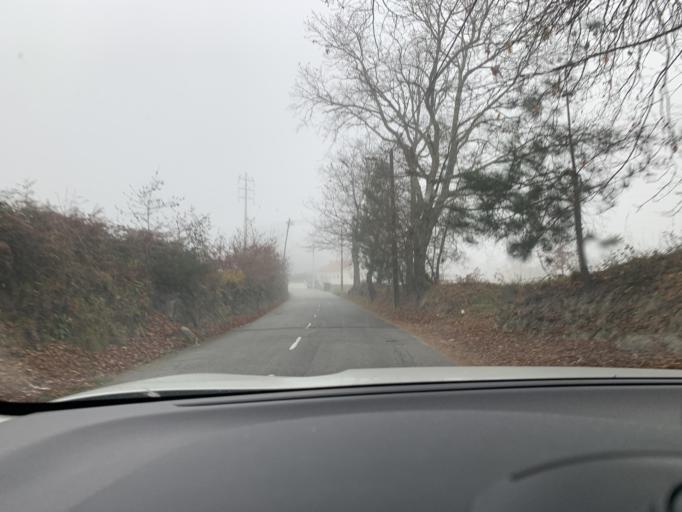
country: PT
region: Viseu
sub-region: Viseu
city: Viseu
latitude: 40.6325
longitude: -7.9199
